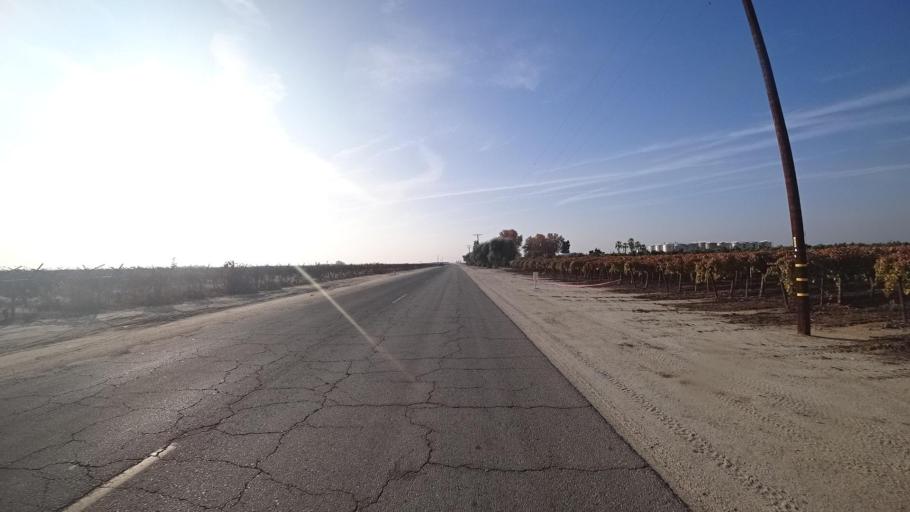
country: US
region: California
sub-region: Kern County
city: Delano
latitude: 35.7863
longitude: -119.1875
